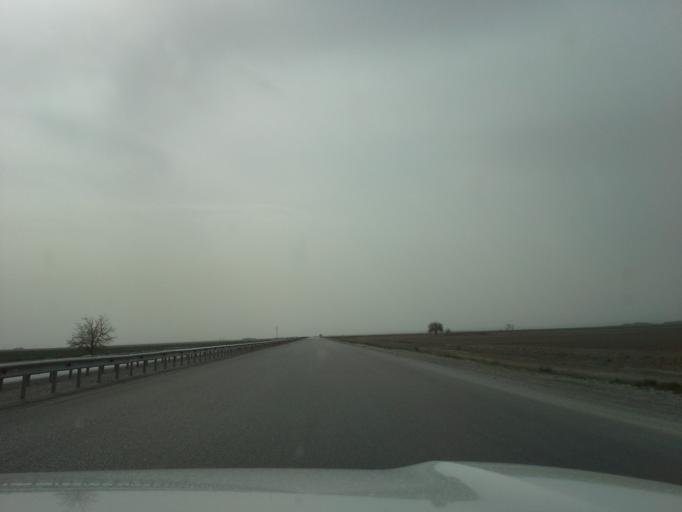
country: TM
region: Ahal
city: Kaka
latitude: 37.4606
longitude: 59.5082
